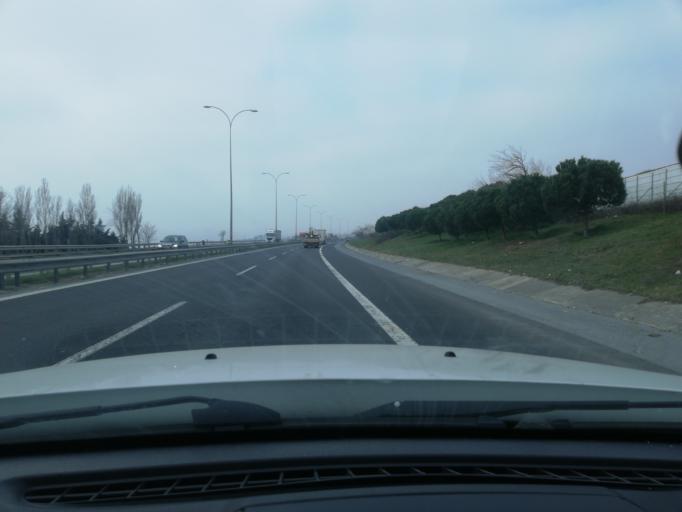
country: TR
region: Istanbul
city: Celaliye
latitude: 41.0508
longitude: 28.4439
